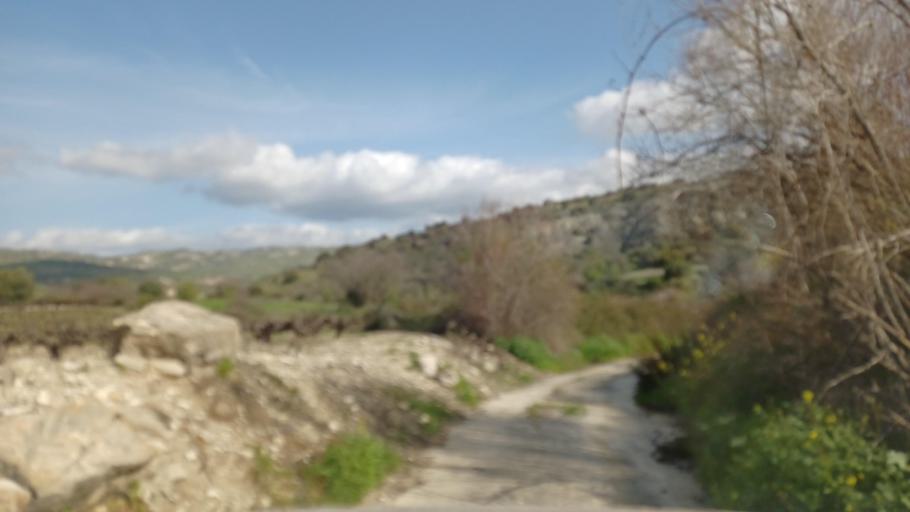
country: CY
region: Limassol
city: Pissouri
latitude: 34.7600
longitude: 32.6419
